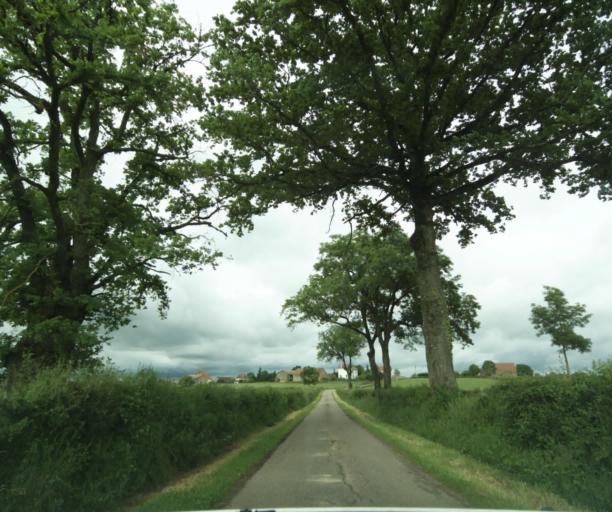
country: FR
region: Bourgogne
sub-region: Departement de Saone-et-Loire
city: Charolles
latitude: 46.4237
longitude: 4.3094
